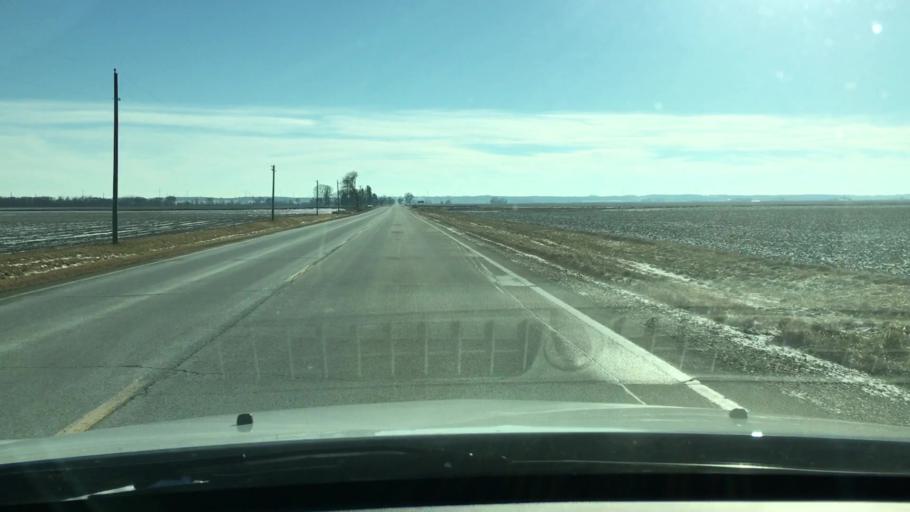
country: US
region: Illinois
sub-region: Ogle County
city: Rochelle
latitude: 41.7912
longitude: -89.0836
